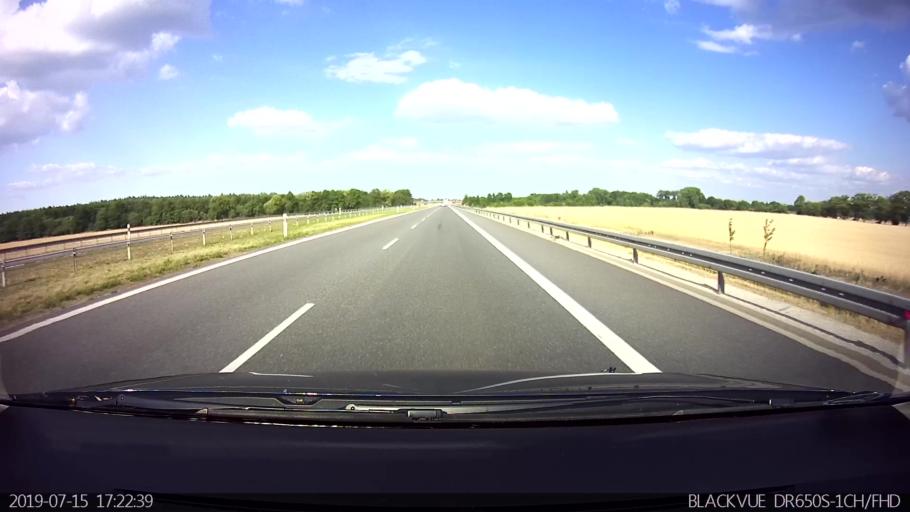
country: PL
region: Greater Poland Voivodeship
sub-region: Powiat kepinski
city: Kepno
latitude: 51.3157
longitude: 17.9626
